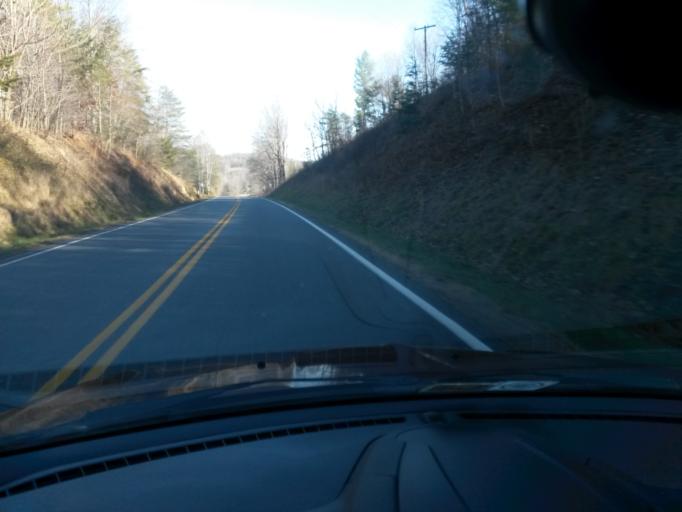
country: US
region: Virginia
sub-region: Patrick County
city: Patrick Springs
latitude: 36.7401
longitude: -80.2097
